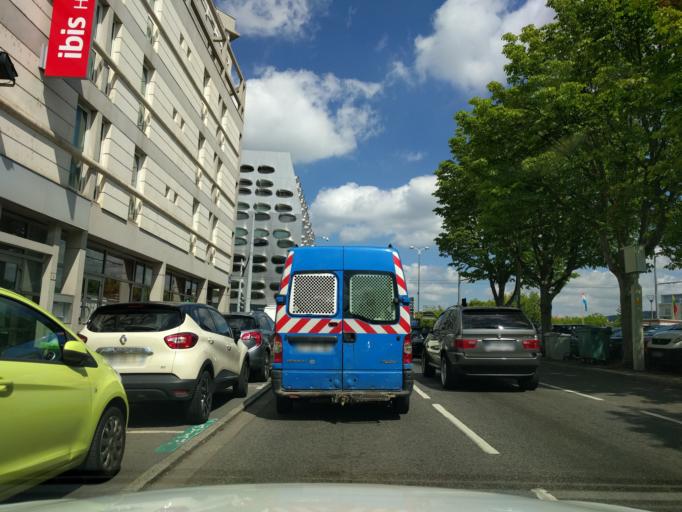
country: FR
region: Lorraine
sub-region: Departement de Meurthe-et-Moselle
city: Nancy
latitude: 48.6934
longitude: 6.1922
